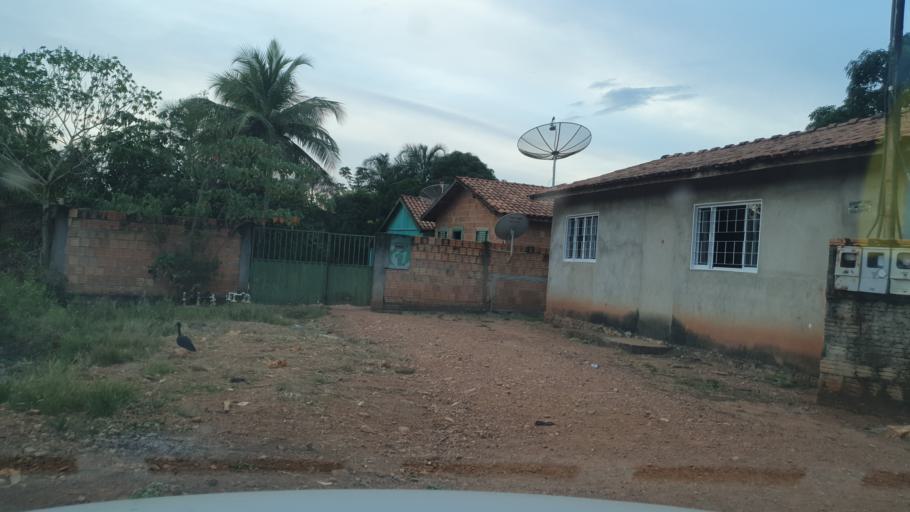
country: BR
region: Mato Grosso
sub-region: Pontes E Lacerda
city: Pontes e Lacerda
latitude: -15.2217
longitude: -59.3510
